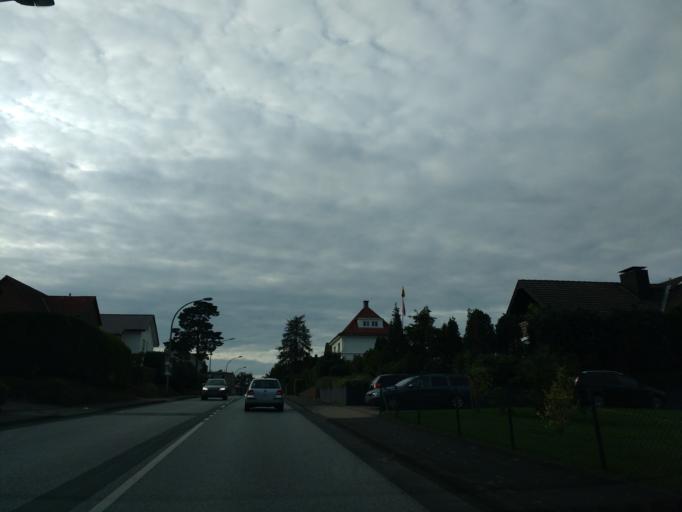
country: DE
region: North Rhine-Westphalia
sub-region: Regierungsbezirk Detmold
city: Lage
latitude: 51.9399
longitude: 8.8057
